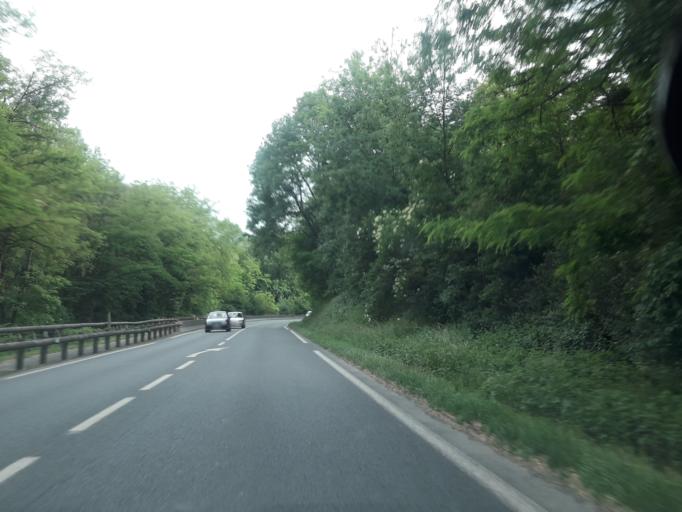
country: FR
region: Rhone-Alpes
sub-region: Departement du Rhone
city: Sain-Bel
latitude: 45.8207
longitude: 4.6054
